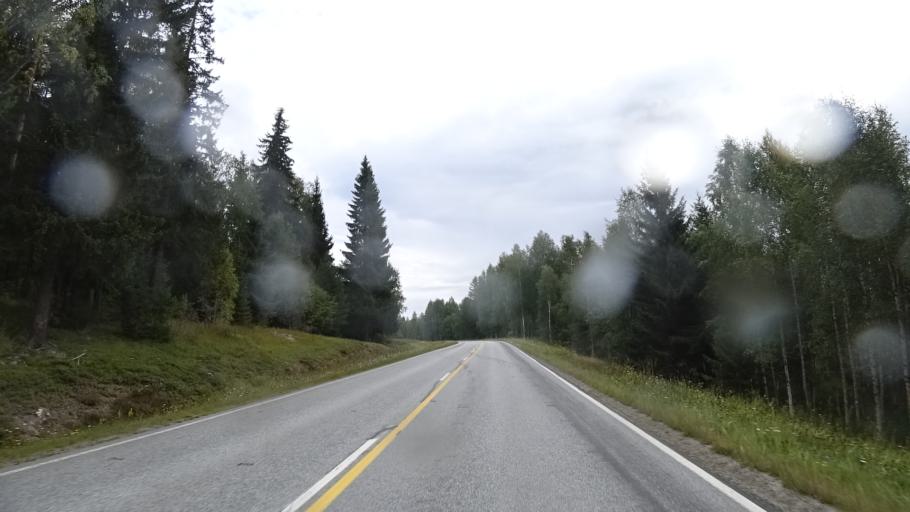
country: FI
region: North Karelia
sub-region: Keski-Karjala
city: Raeaekkylae
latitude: 62.1069
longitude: 29.6994
